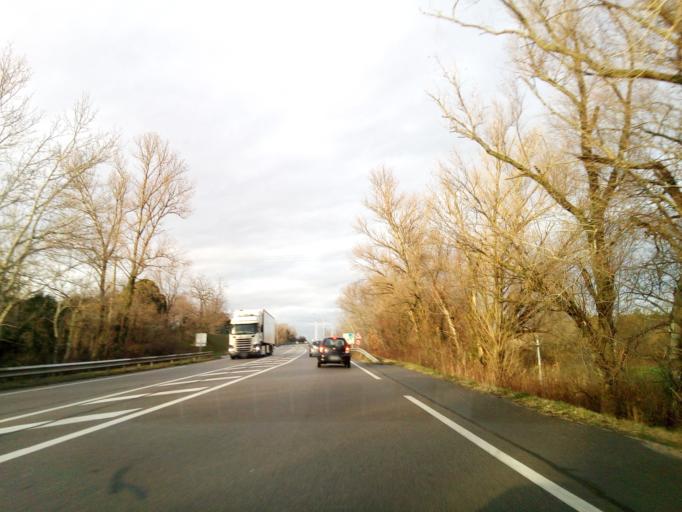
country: FR
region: Rhone-Alpes
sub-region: Departement de la Drome
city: Portes-les-Valence
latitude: 44.8691
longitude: 4.8626
